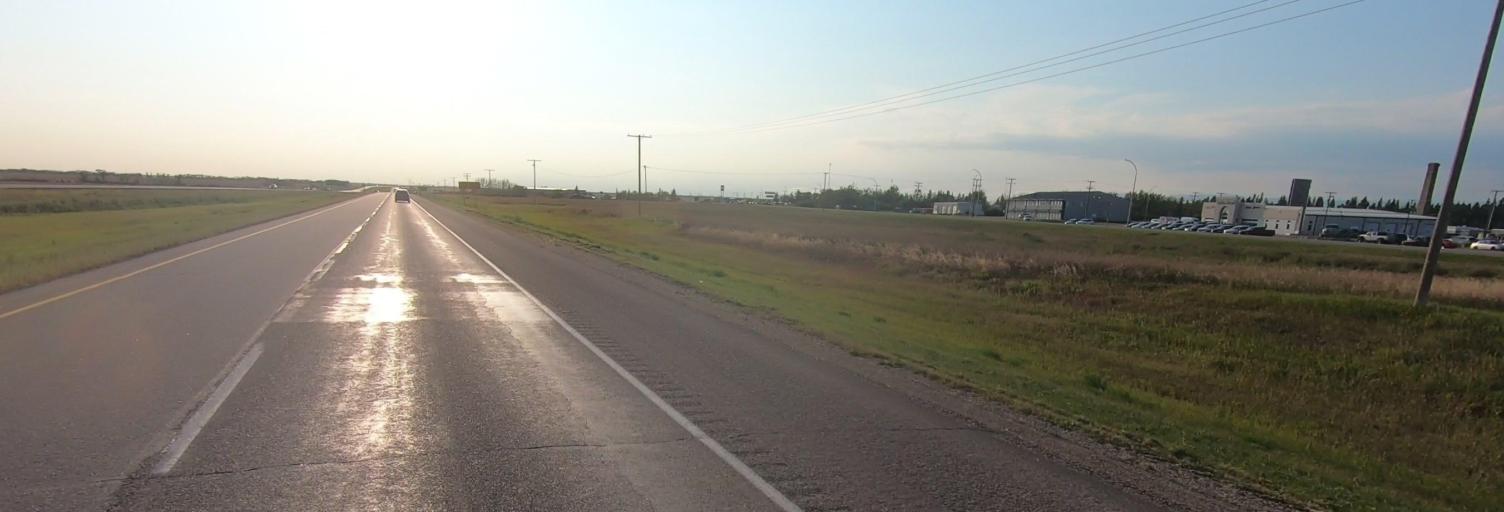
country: CA
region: Saskatchewan
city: Indian Head
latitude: 50.5255
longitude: -103.6670
